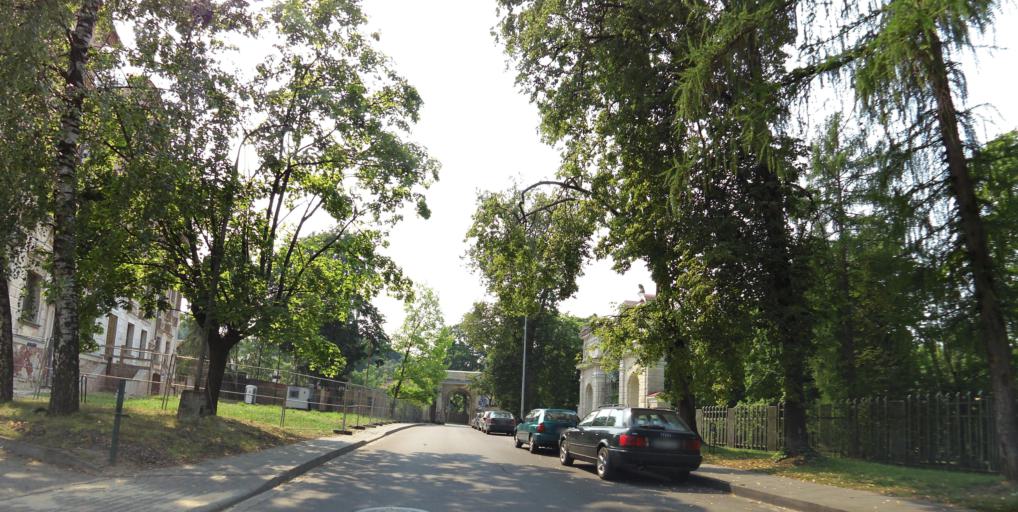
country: LT
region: Vilnius County
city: Rasos
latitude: 54.6990
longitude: 25.3135
